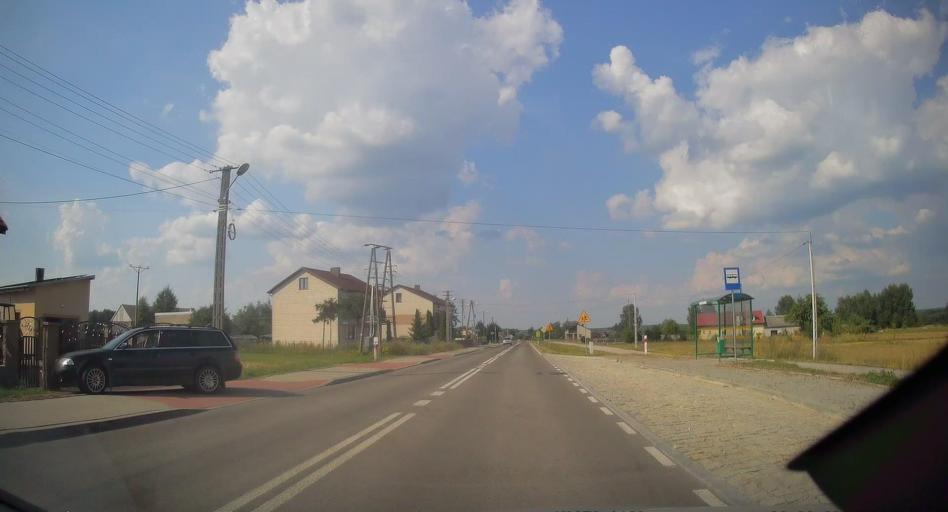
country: PL
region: Swietokrzyskie
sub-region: Powiat konecki
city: Radoszyce
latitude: 51.0427
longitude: 20.2831
